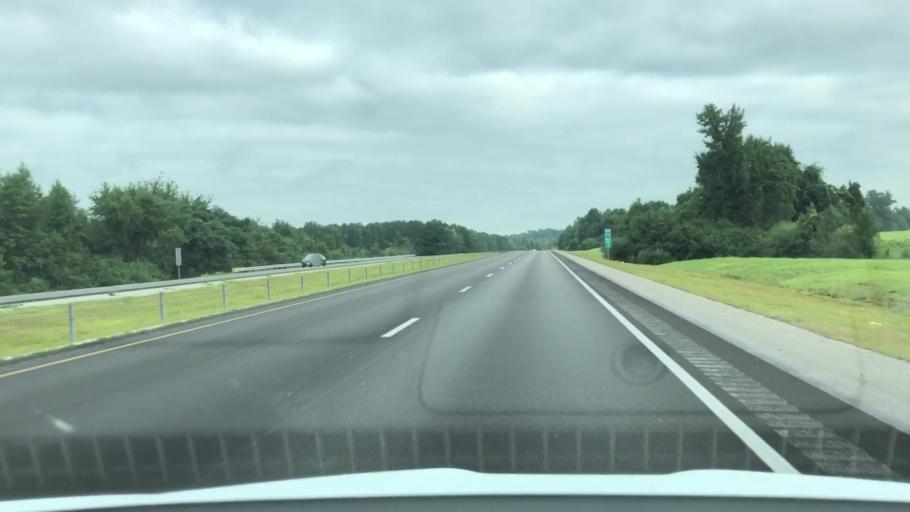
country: US
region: North Carolina
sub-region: Wayne County
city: Fremont
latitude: 35.5753
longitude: -77.9894
